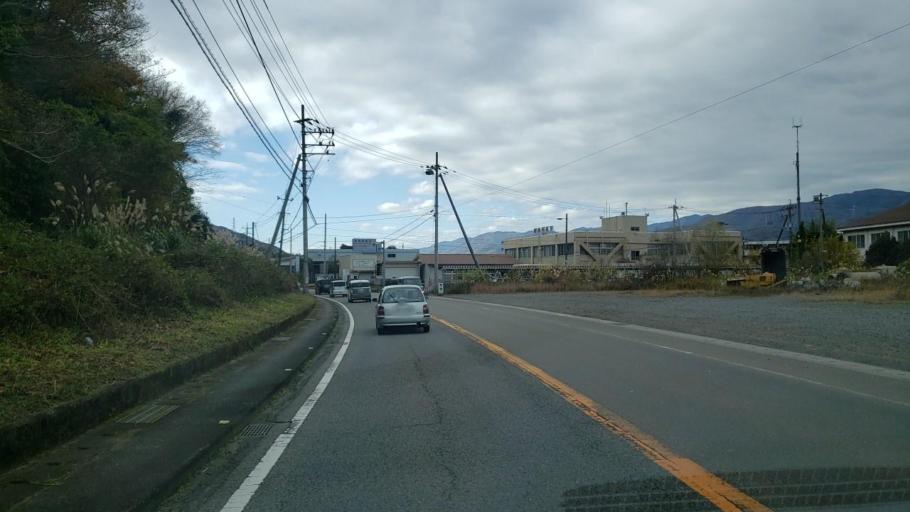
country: JP
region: Tokushima
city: Wakimachi
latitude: 34.0564
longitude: 134.1579
